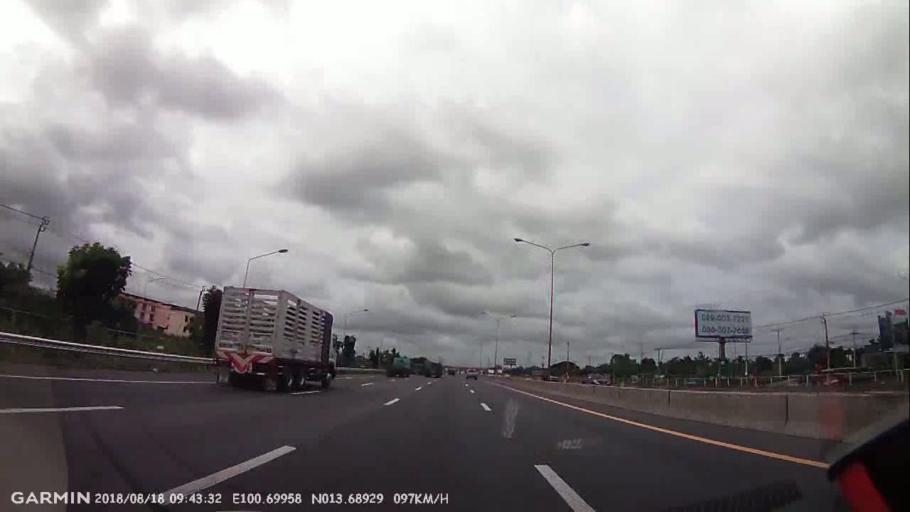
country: TH
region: Bangkok
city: Bang Na
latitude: 13.6891
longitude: 100.6996
